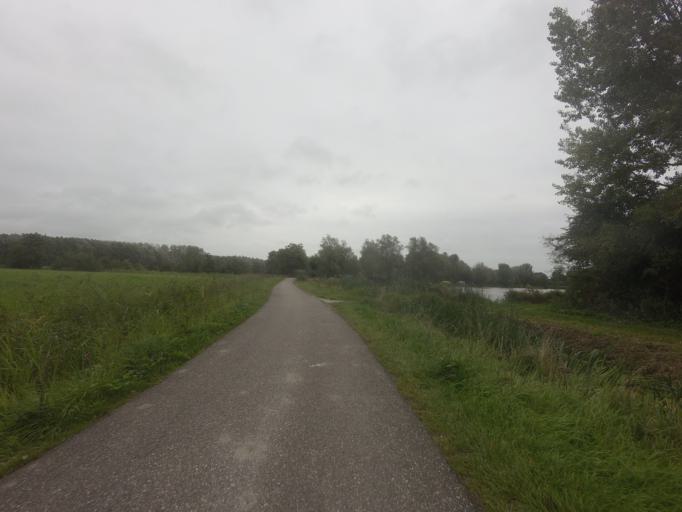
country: NL
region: Friesland
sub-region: Gemeente Leeuwarden
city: Bilgaard
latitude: 53.2203
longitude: 5.7900
